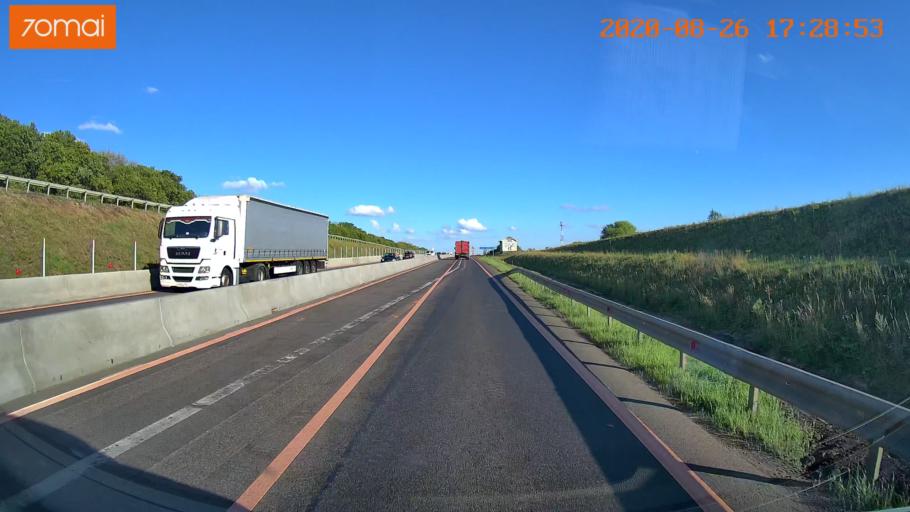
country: RU
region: Tula
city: Kazachka
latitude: 53.4591
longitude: 38.1424
